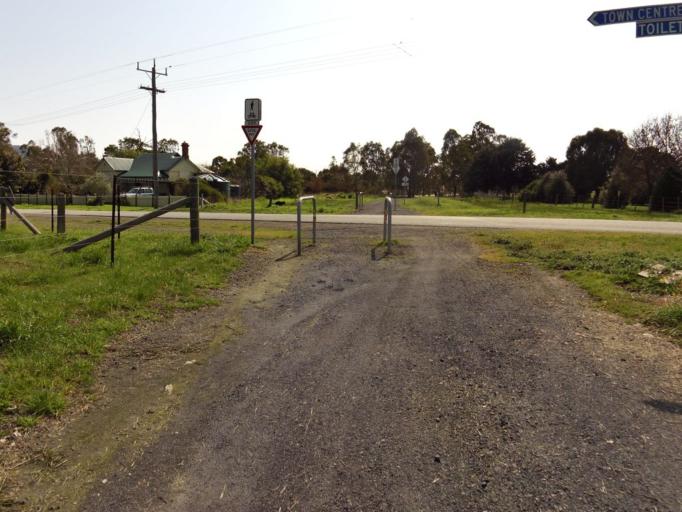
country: AU
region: Victoria
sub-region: Murrindindi
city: Alexandra
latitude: -37.1014
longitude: 145.6185
